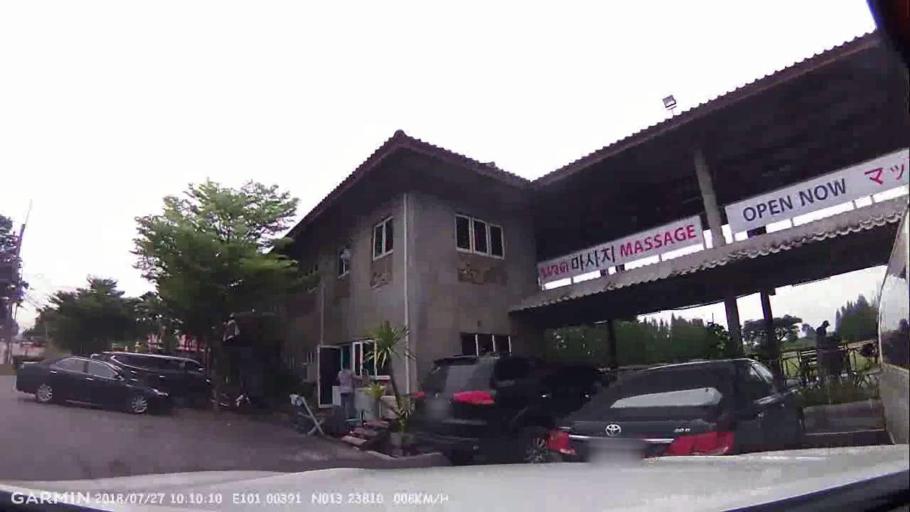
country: TH
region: Chon Buri
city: Si Racha
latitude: 13.2381
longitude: 101.0039
